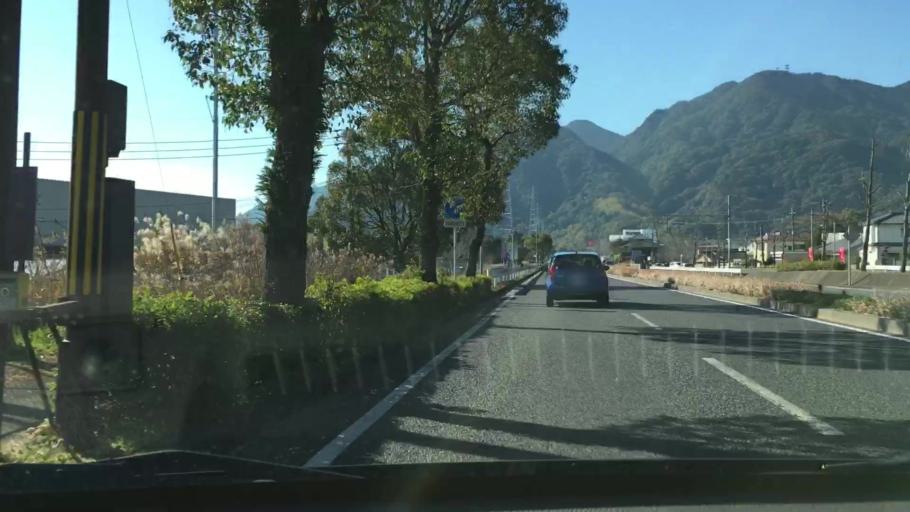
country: JP
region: Kagoshima
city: Kajiki
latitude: 31.7131
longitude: 130.6174
